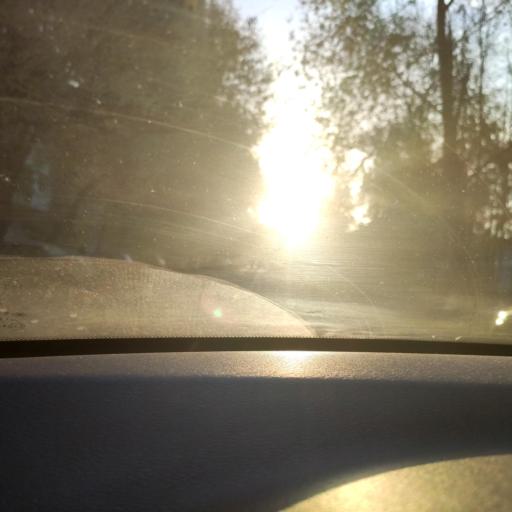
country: RU
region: Samara
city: Petra-Dubrava
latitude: 53.2347
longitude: 50.2830
